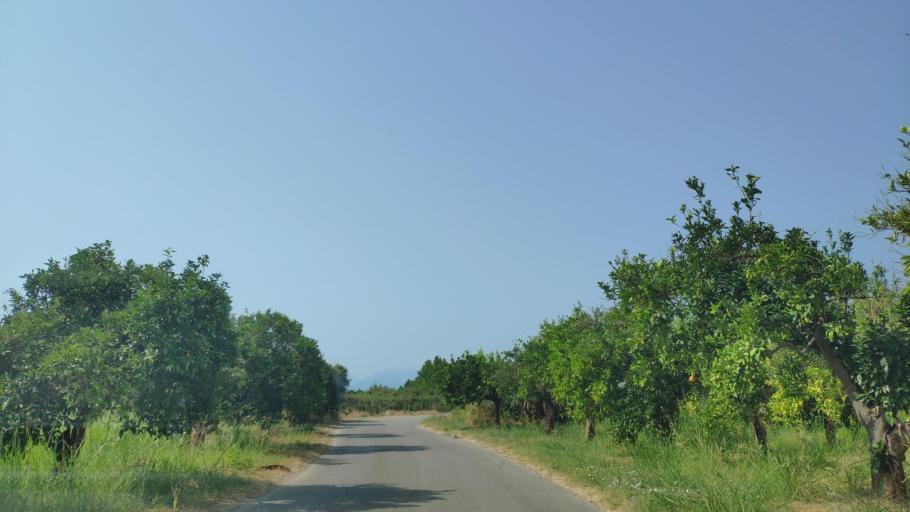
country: GR
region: Epirus
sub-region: Nomos Artas
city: Kompoti
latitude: 39.0780
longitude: 21.0846
